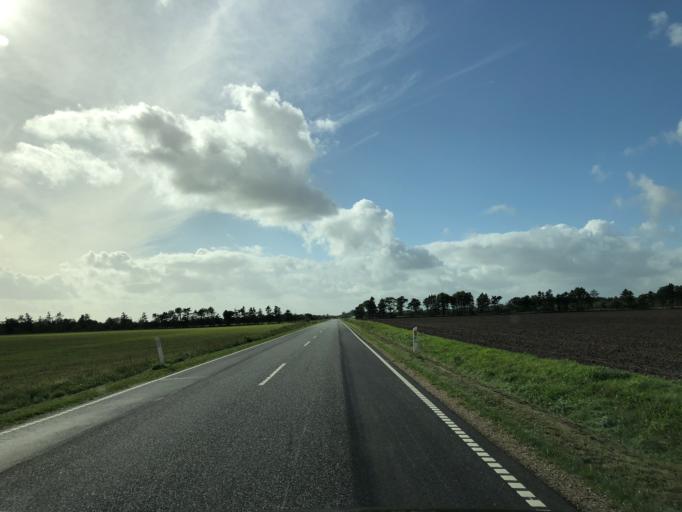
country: DK
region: Central Jutland
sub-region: Holstebro Kommune
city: Holstebro
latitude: 56.3690
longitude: 8.4710
